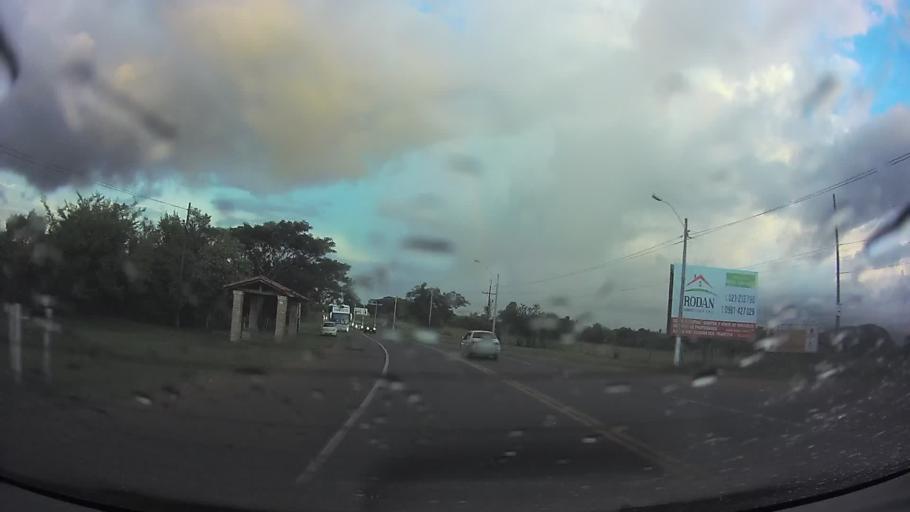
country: PY
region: Paraguari
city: Yaguaron
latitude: -25.5749
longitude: -57.2781
